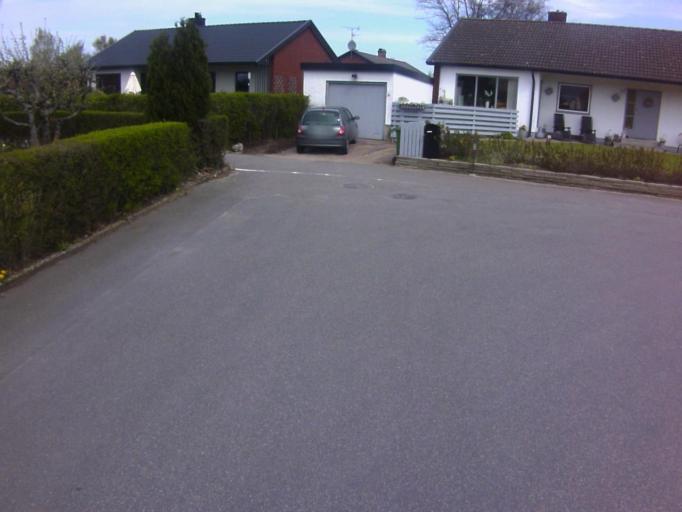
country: SE
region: Skane
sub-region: Kavlinge Kommun
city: Loddekopinge
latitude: 55.7542
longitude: 13.0071
